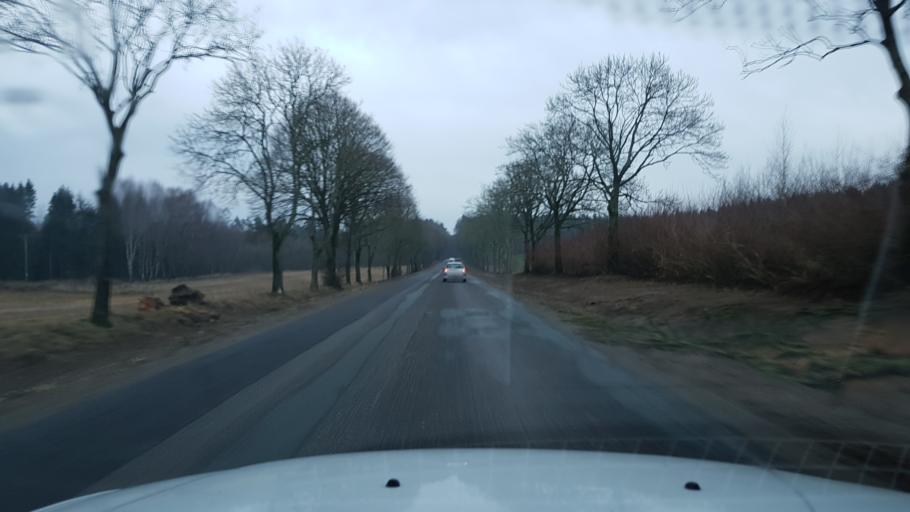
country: PL
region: West Pomeranian Voivodeship
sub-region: Powiat gryficki
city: Gryfice
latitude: 53.8633
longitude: 15.2217
